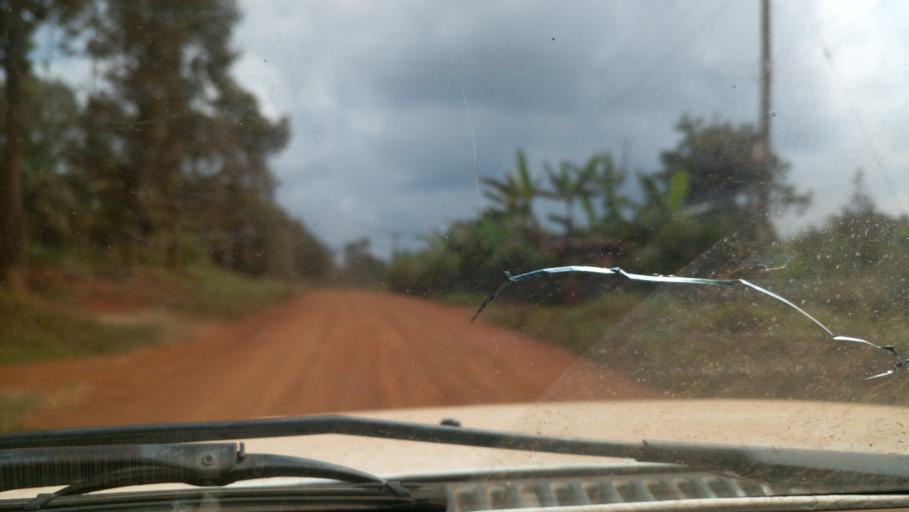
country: KE
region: Nairobi Area
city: Thika
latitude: -0.8950
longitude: 36.9486
